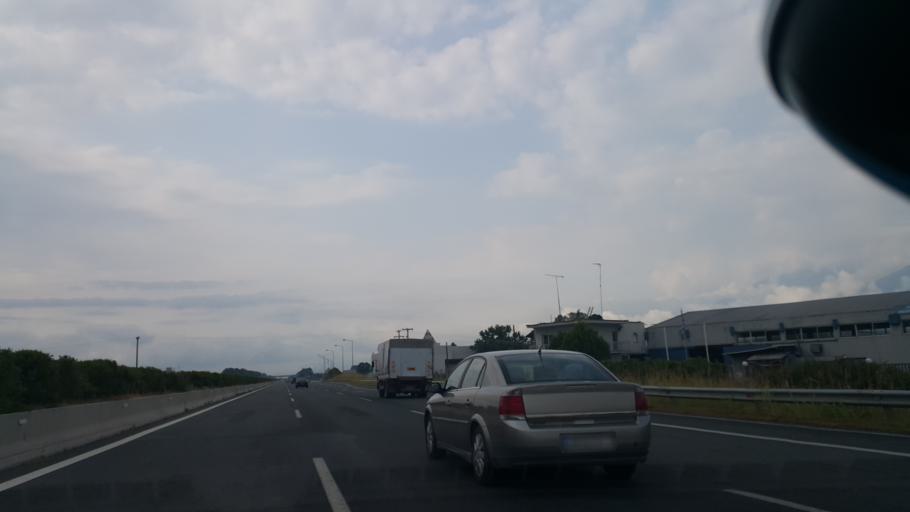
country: GR
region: Central Macedonia
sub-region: Nomos Pierias
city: Peristasi
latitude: 40.2397
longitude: 22.5361
